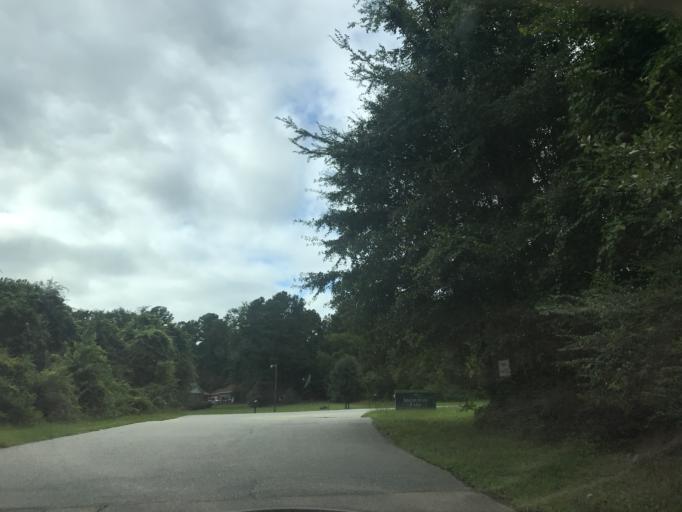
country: US
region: North Carolina
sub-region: Wake County
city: Knightdale
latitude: 35.7999
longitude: -78.5423
